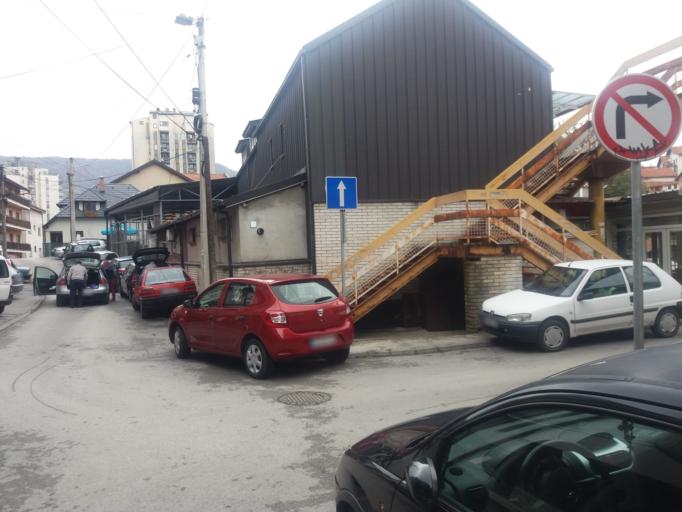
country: RS
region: Central Serbia
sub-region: Zlatiborski Okrug
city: Uzice
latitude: 43.8580
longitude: 19.8487
